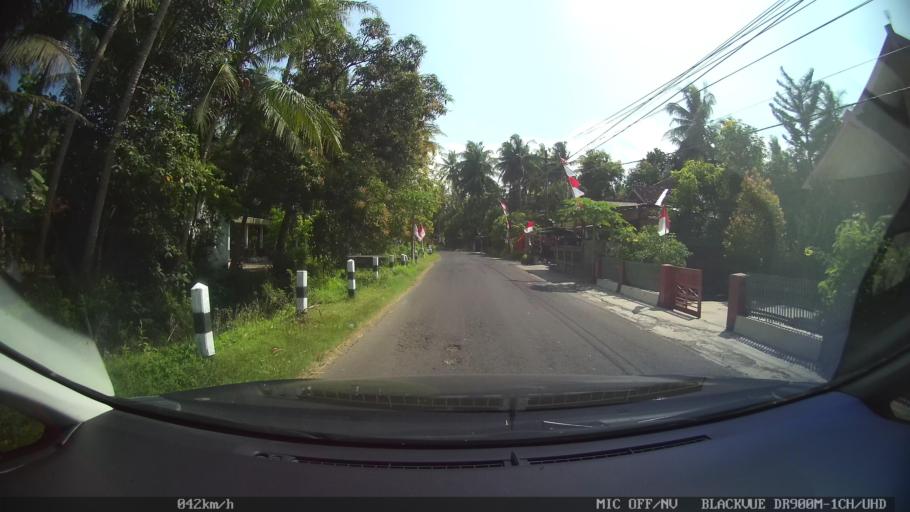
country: ID
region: Daerah Istimewa Yogyakarta
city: Srandakan
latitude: -7.9128
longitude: 110.1539
